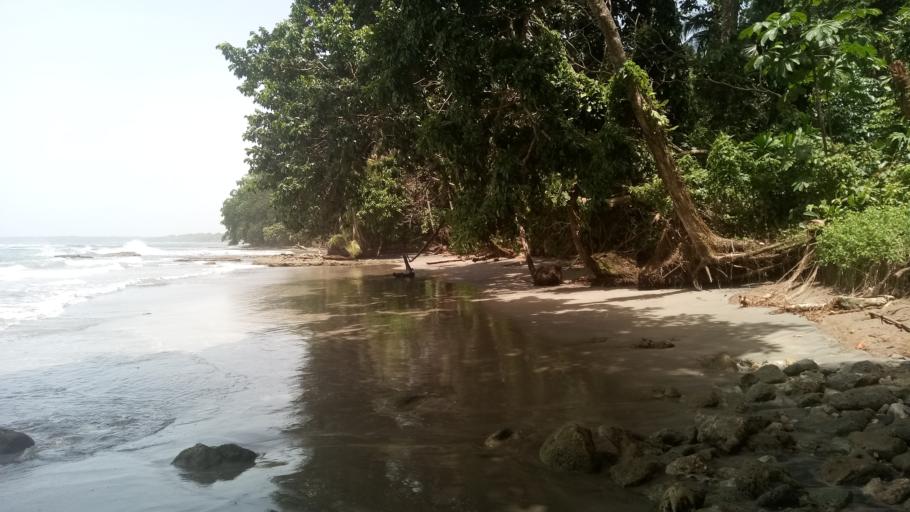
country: CR
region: Limon
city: Sixaola
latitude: 9.6266
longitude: -82.6200
